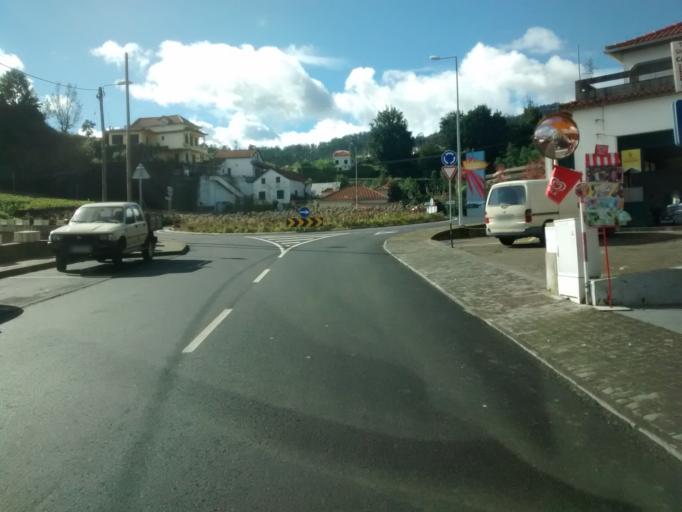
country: PT
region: Madeira
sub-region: Santana
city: Santana
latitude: 32.8058
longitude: -16.8850
